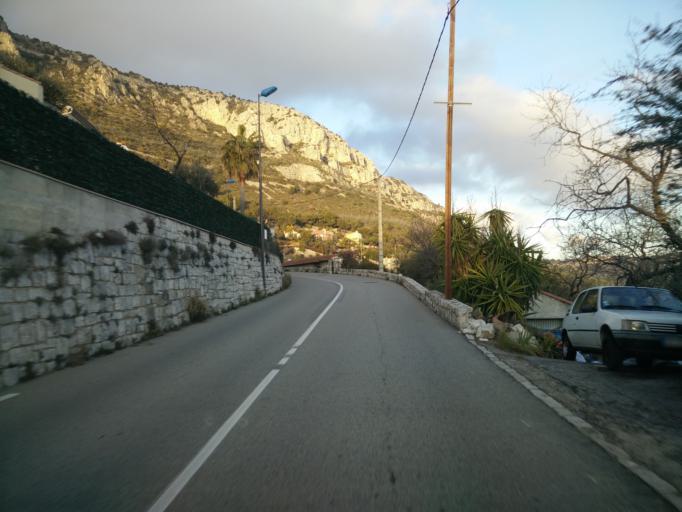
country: FR
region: Provence-Alpes-Cote d'Azur
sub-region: Departement des Alpes-Maritimes
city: Eze
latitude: 43.7300
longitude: 7.3722
